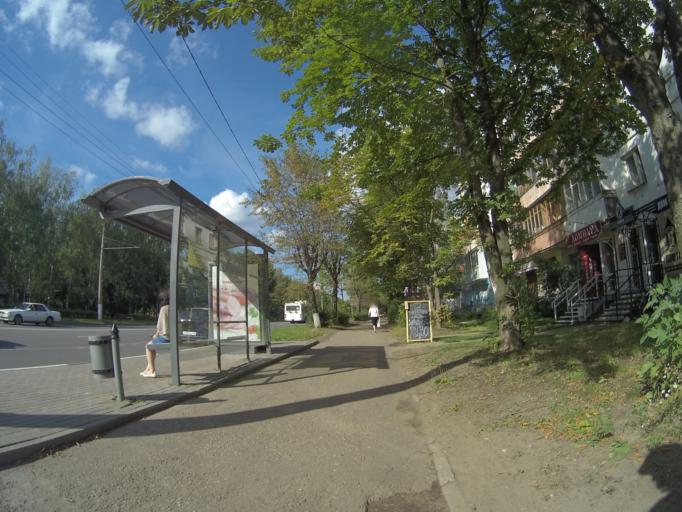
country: RU
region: Vladimir
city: Vladimir
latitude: 56.1341
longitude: 40.3601
